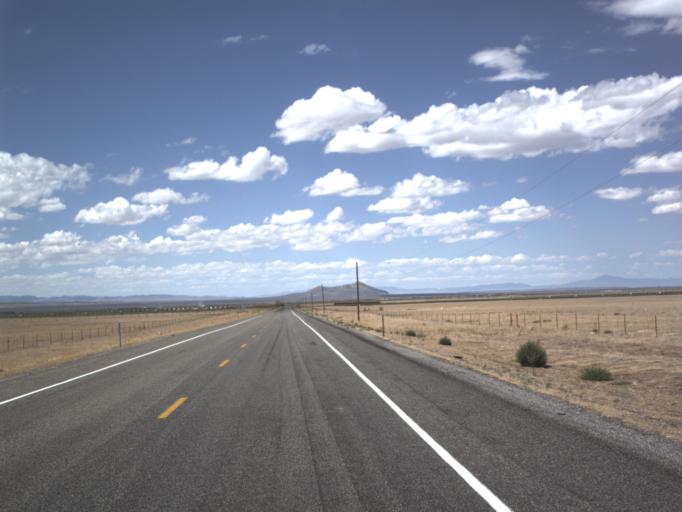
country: US
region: Utah
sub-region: Millard County
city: Fillmore
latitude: 39.1181
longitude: -112.3185
